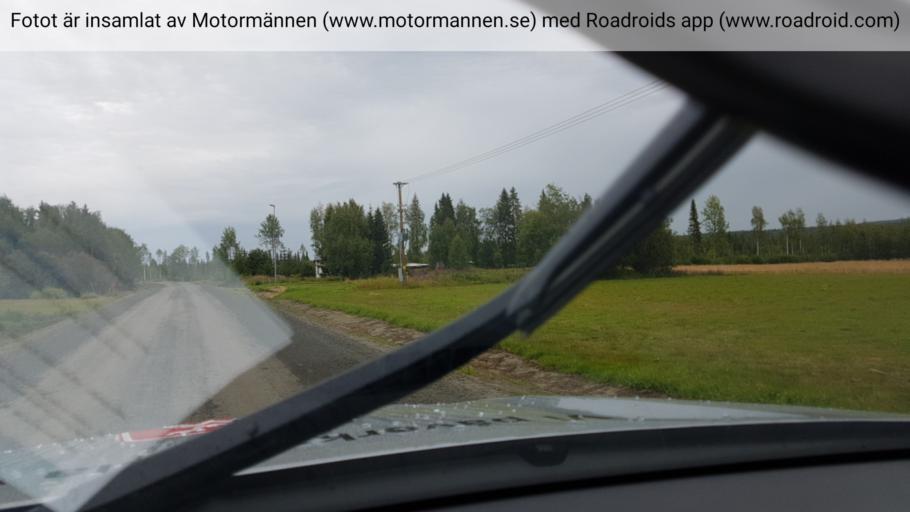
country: SE
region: Norrbotten
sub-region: Alvsbyns Kommun
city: AElvsbyn
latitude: 65.9200
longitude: 21.2666
